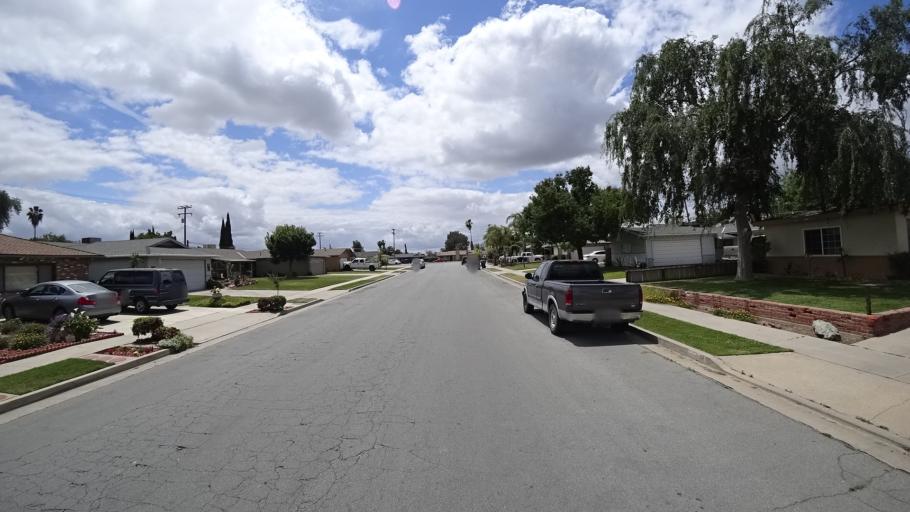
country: US
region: California
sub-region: Kings County
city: Hanford
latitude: 36.3365
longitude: -119.6275
